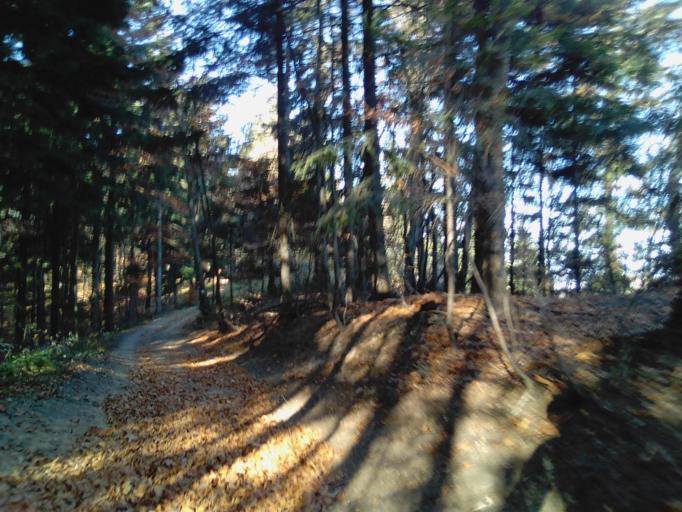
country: PL
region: Subcarpathian Voivodeship
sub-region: Powiat strzyzowski
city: Wysoka Strzyzowska
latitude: 49.8132
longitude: 21.7143
